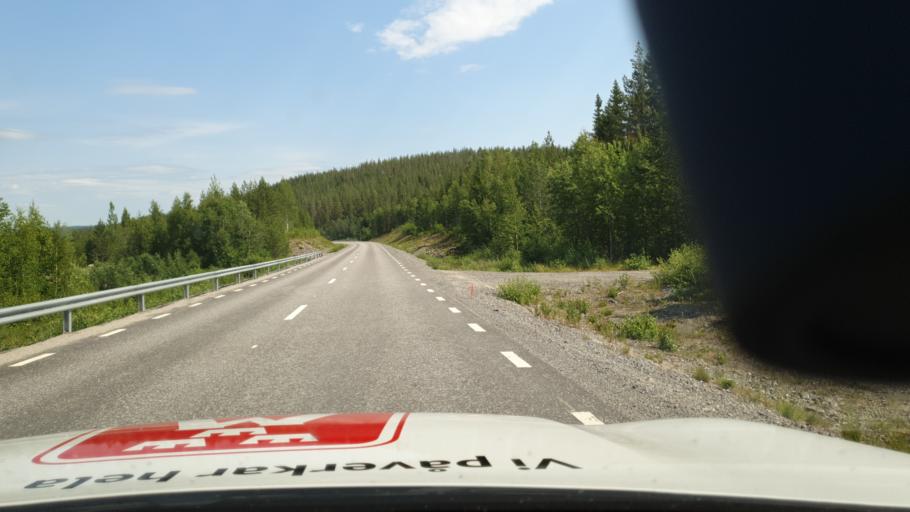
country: SE
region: Vaesterbotten
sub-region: Vindelns Kommun
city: Vindeln
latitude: 64.2477
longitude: 20.1067
